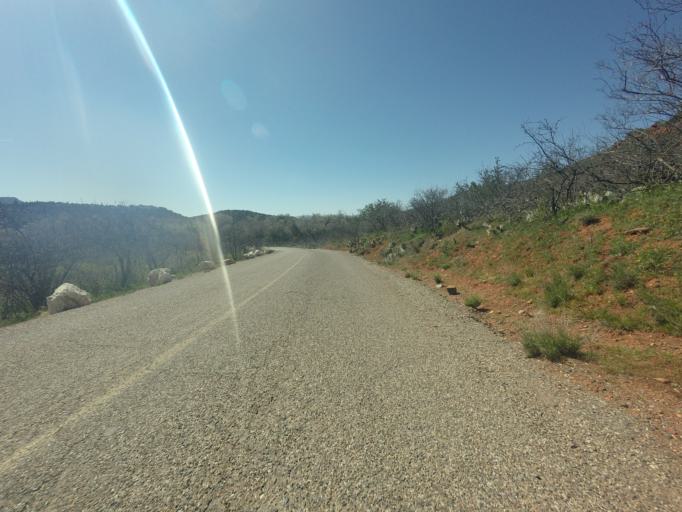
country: US
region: Arizona
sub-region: Yavapai County
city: Lake Montezuma
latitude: 34.6711
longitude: -111.7150
